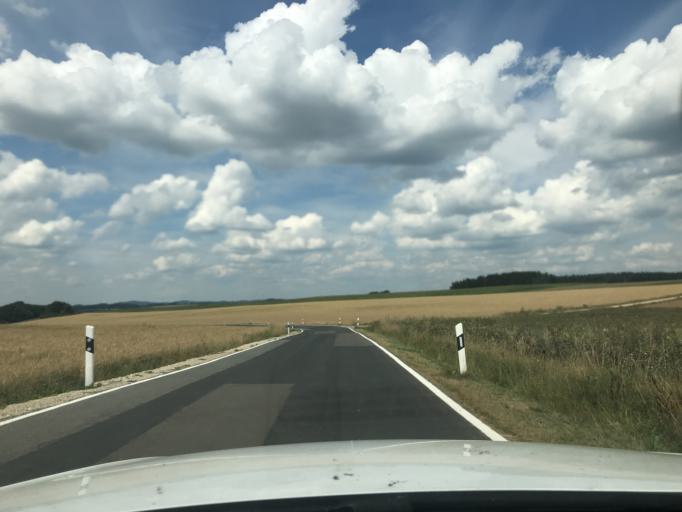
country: DE
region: Bavaria
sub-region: Upper Palatinate
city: Auerbach
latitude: 49.7379
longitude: 11.6499
